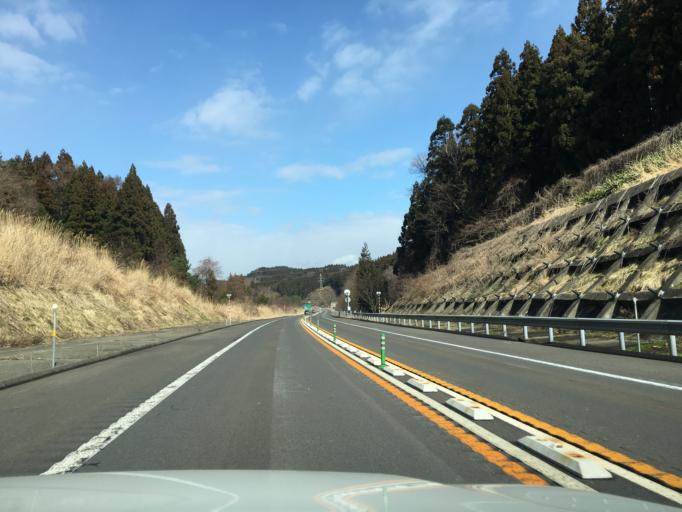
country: JP
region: Akita
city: Akita
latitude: 39.7693
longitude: 140.1214
